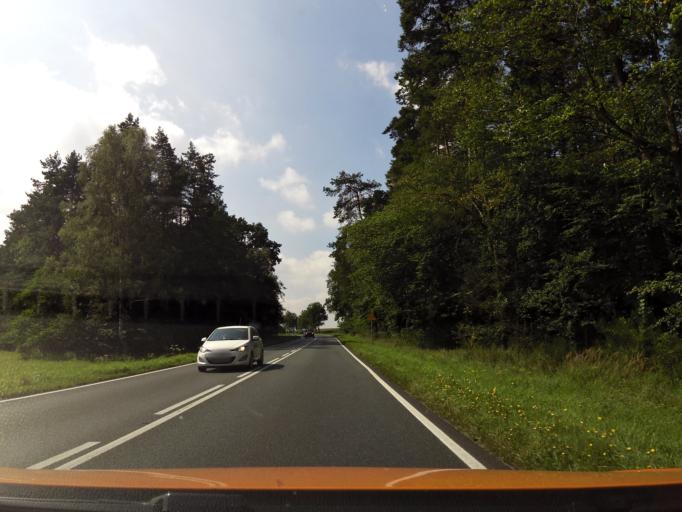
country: PL
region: West Pomeranian Voivodeship
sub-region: Powiat gryficki
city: Ploty
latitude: 53.7582
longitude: 15.2277
